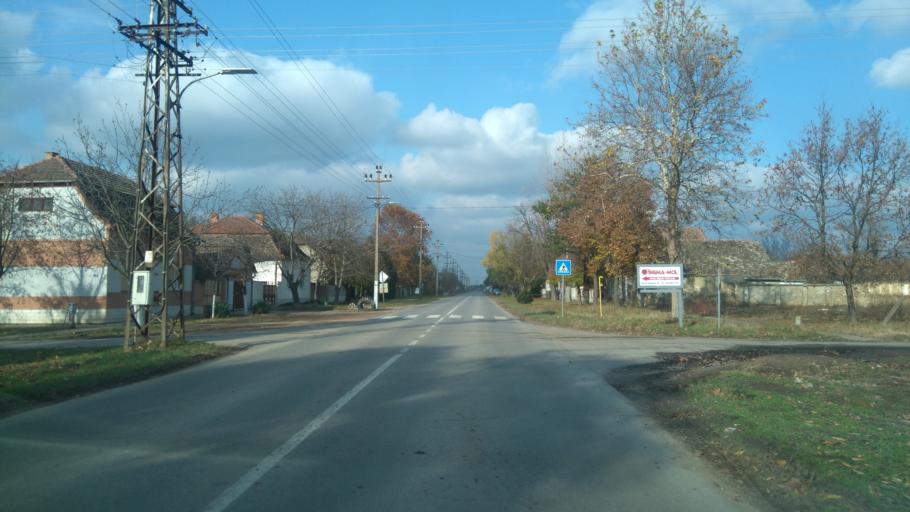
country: RS
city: Mol
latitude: 45.7676
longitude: 20.1291
